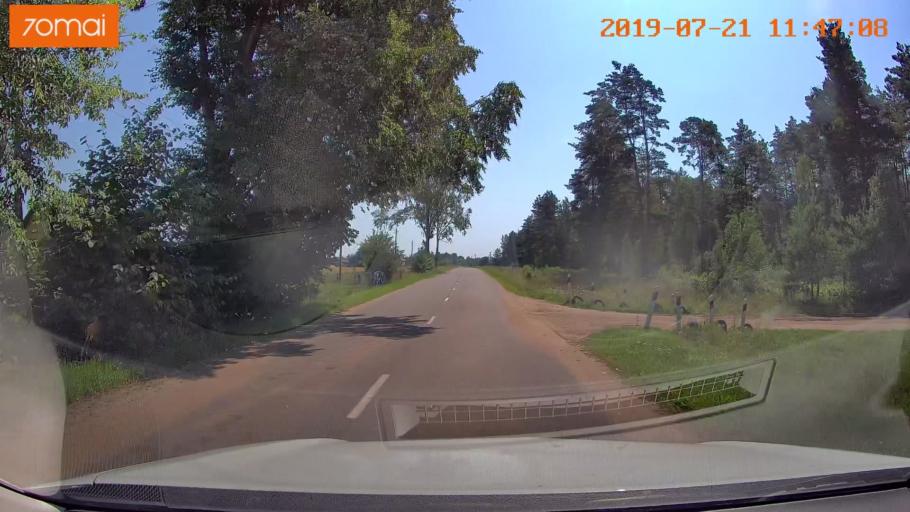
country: BY
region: Grodnenskaya
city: Lyubcha
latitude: 53.9042
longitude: 26.0419
